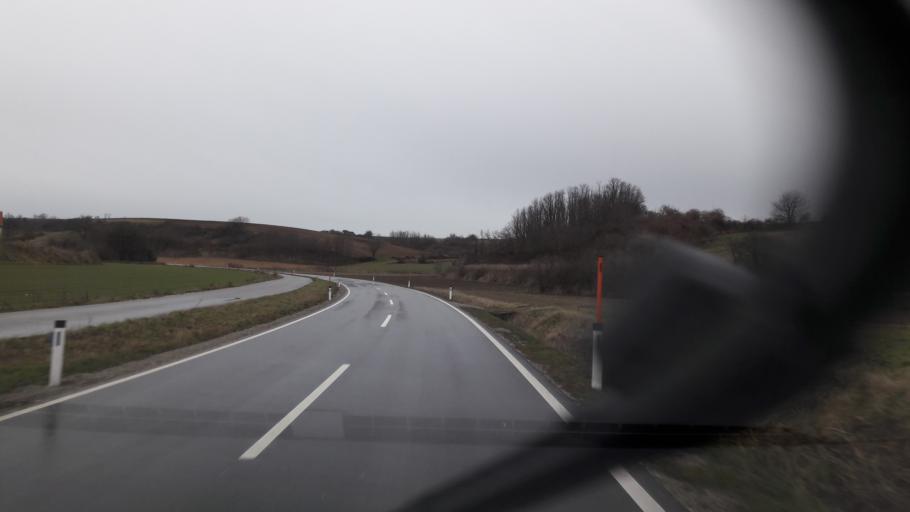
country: AT
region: Lower Austria
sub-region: Politischer Bezirk Mistelbach
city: Hochleithen
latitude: 48.4386
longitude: 16.5415
